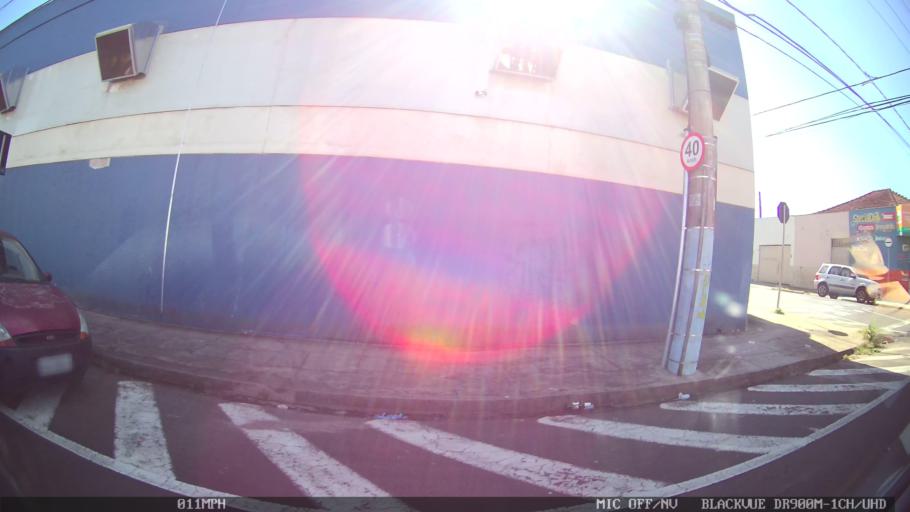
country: BR
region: Sao Paulo
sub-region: Franca
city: Franca
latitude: -20.5470
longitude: -47.3867
